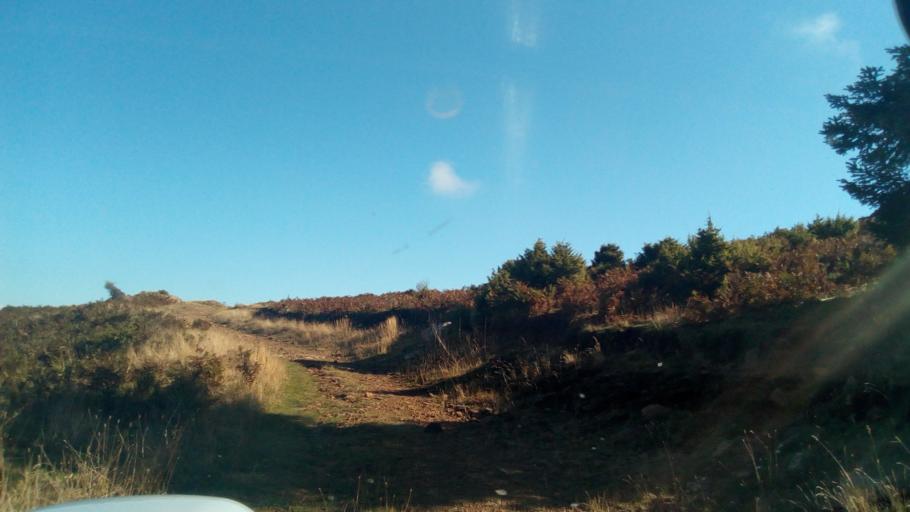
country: GR
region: Central Greece
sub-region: Nomos Fokidos
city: Lidoriki
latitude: 38.6052
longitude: 21.9660
